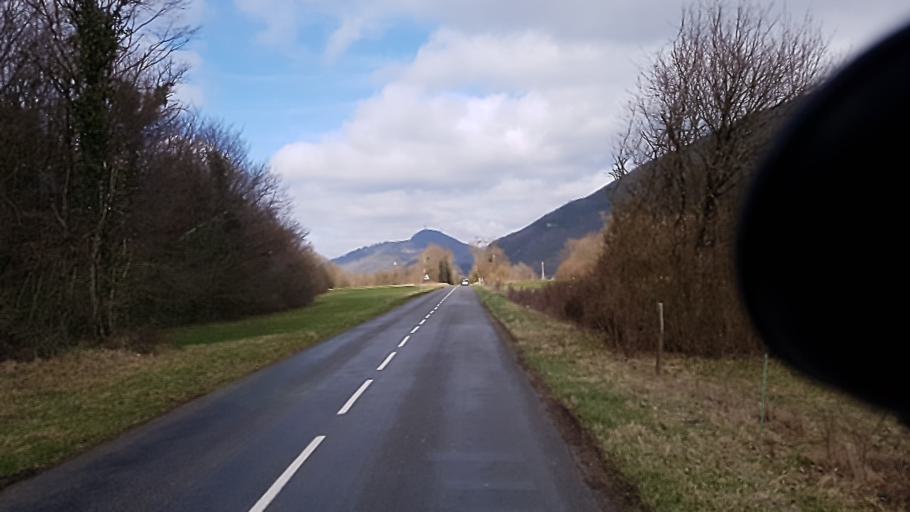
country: FR
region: Rhone-Alpes
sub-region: Departement de l'Ain
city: Izernore
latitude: 46.2491
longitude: 5.5009
